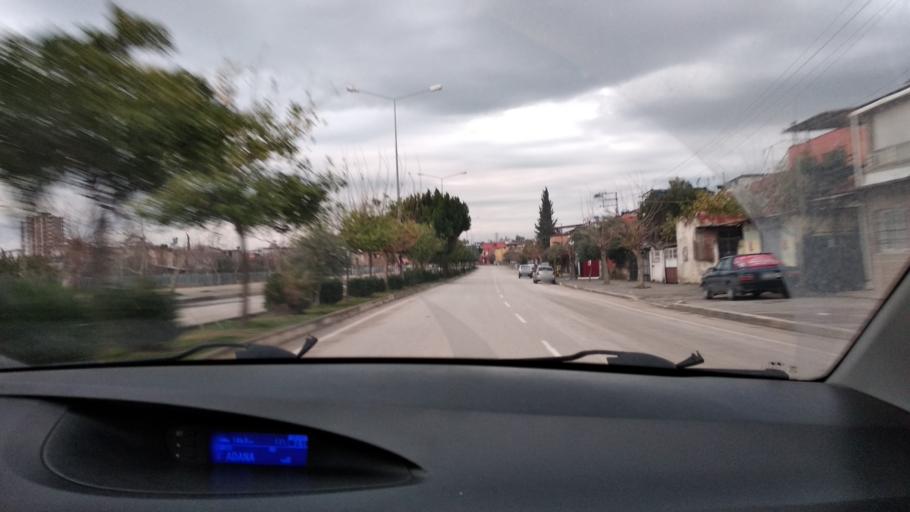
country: TR
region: Adana
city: Yuregir
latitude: 37.0123
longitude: 35.3877
